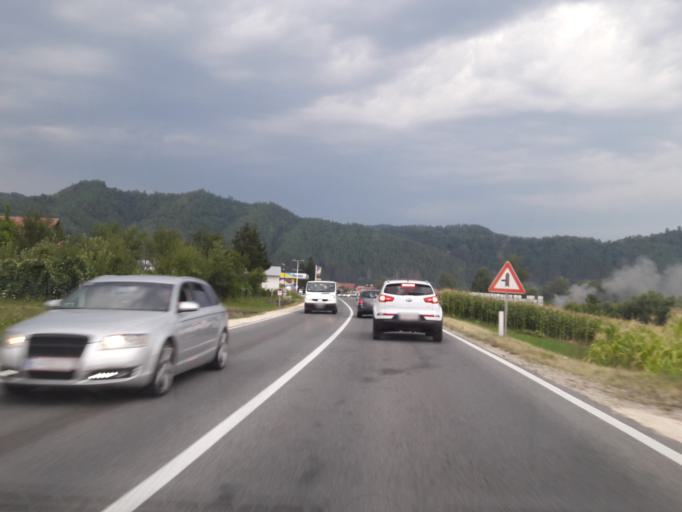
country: BA
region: Federation of Bosnia and Herzegovina
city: Maglaj
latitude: 44.5932
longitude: 18.0932
